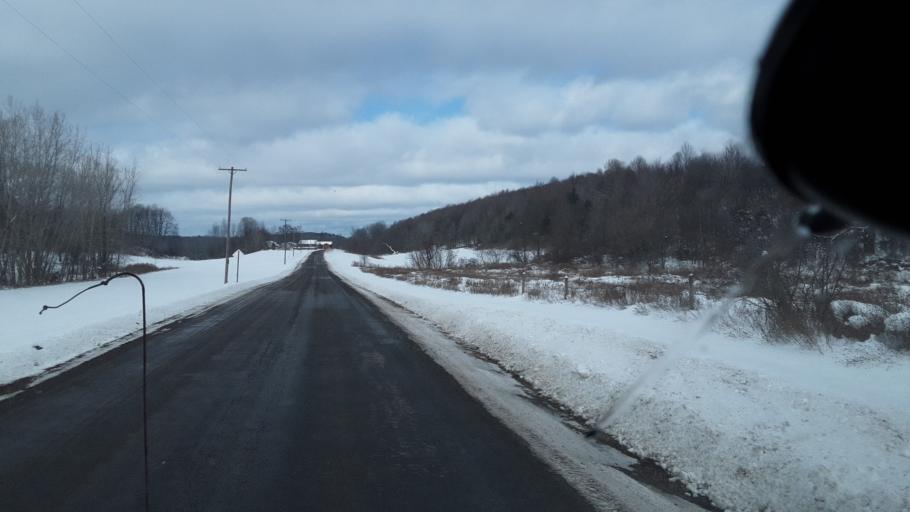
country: US
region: New York
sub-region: Wayne County
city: Lyons
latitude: 43.1057
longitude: -77.0450
